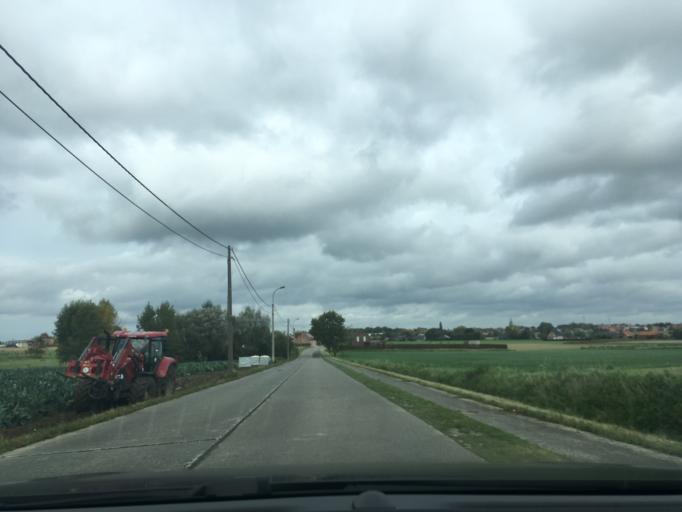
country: BE
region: Flanders
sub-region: Provincie West-Vlaanderen
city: Moorslede
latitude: 50.8783
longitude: 3.0452
